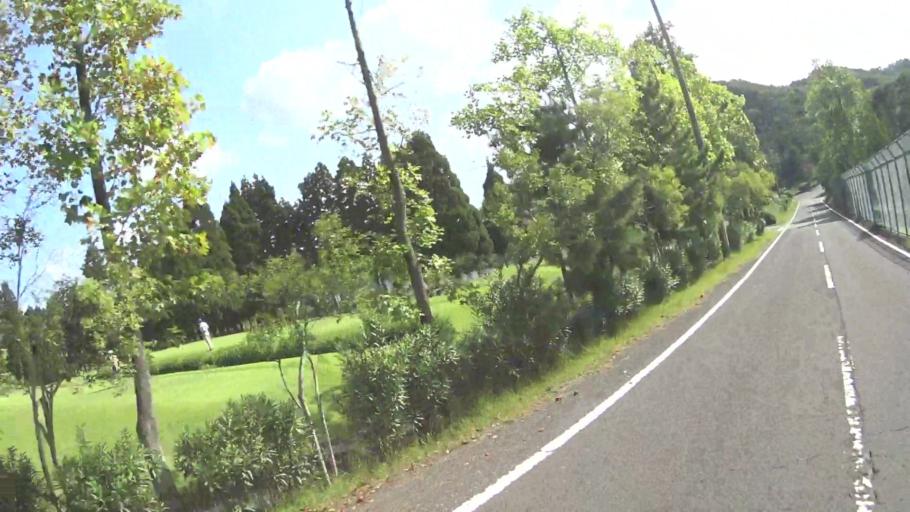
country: JP
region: Kyoto
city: Miyazu
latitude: 35.6273
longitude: 135.2227
